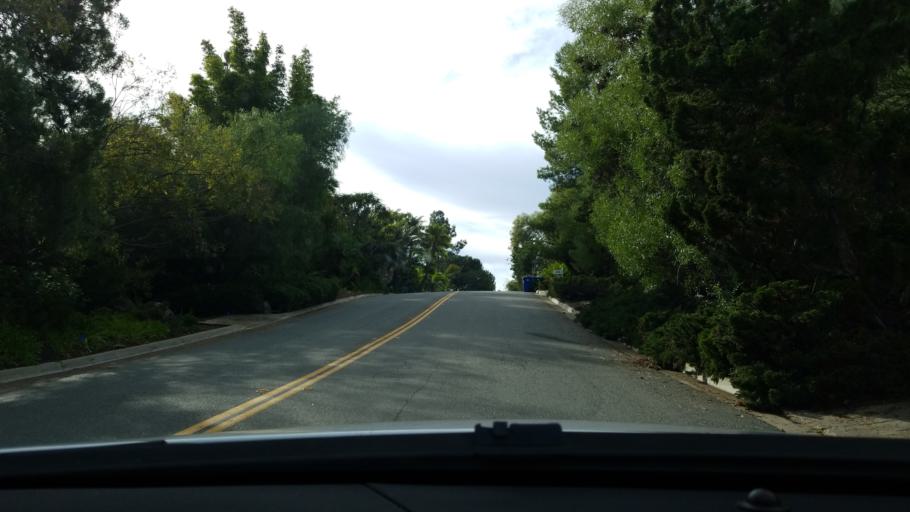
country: US
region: California
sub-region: San Diego County
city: Casa de Oro-Mount Helix
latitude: 32.7670
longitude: -116.9510
